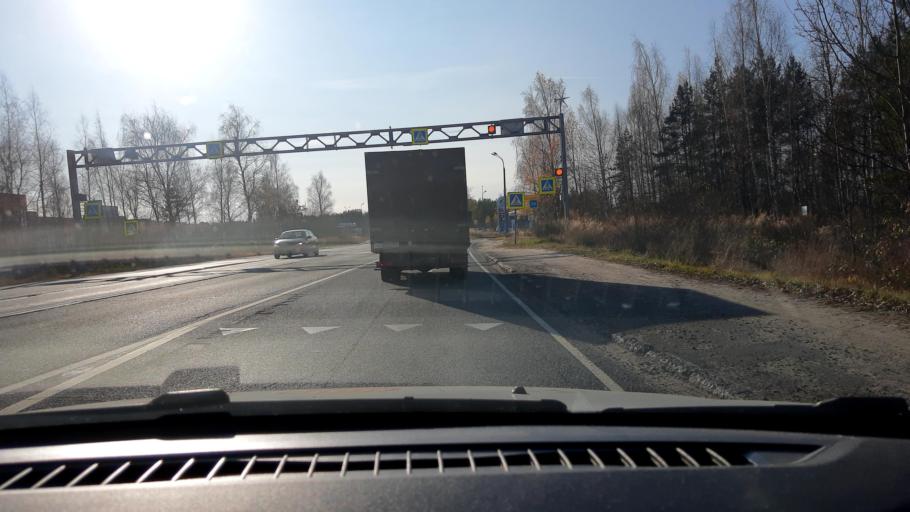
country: RU
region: Nizjnij Novgorod
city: Dzerzhinsk
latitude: 56.2959
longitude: 43.4762
